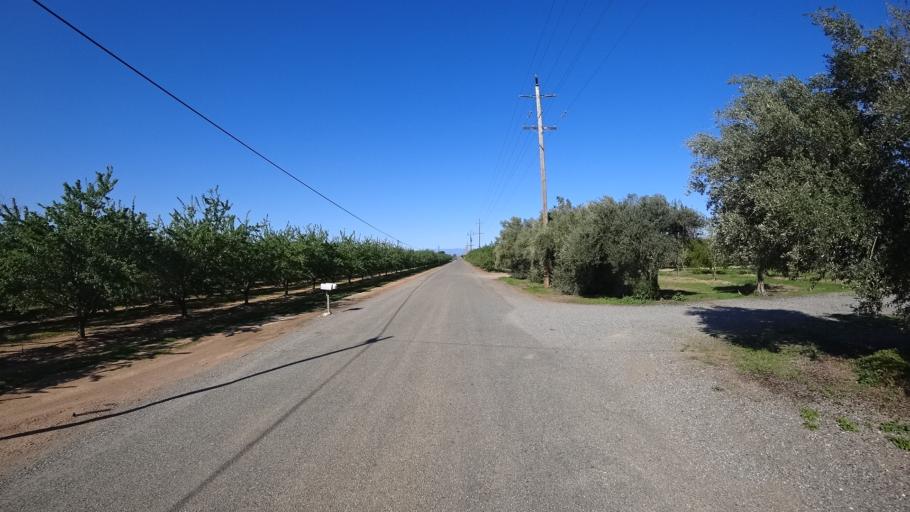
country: US
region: California
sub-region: Glenn County
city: Hamilton City
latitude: 39.7757
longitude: -122.0995
